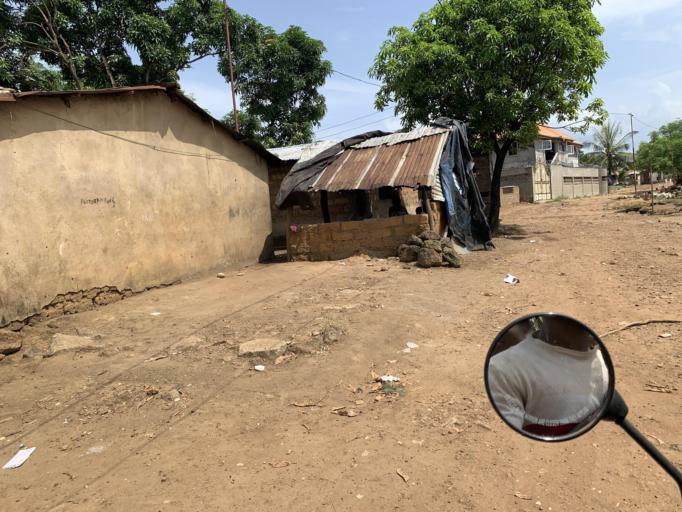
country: SL
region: Western Area
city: Hastings
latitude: 8.4077
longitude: -13.1358
